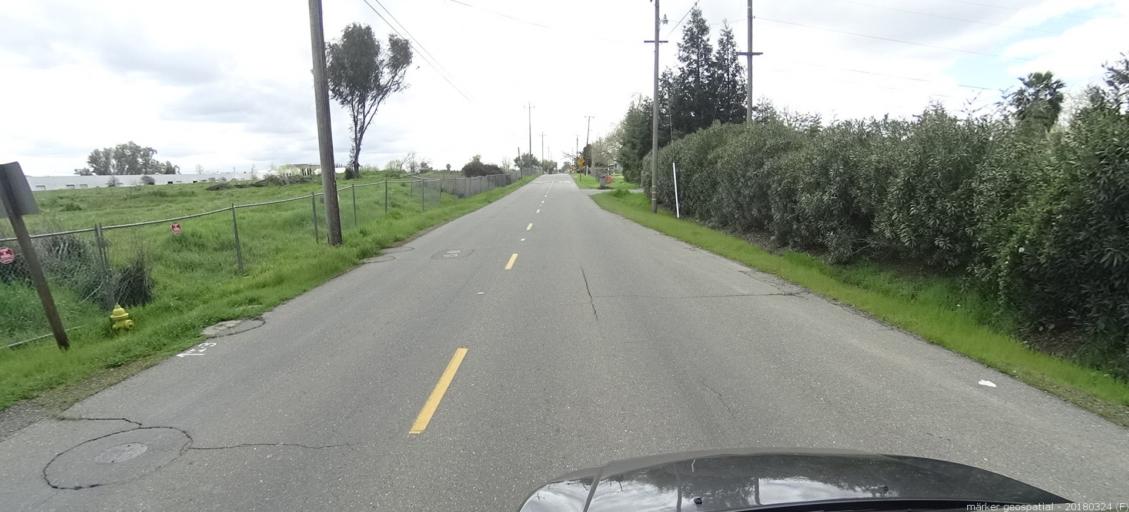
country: US
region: California
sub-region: Sacramento County
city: North Highlands
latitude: 38.6860
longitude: -121.3875
